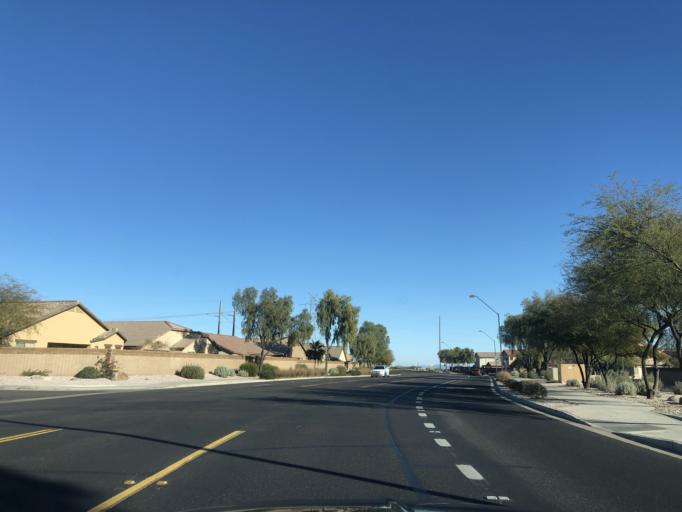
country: US
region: Arizona
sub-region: Maricopa County
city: Buckeye
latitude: 33.4207
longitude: -112.6022
